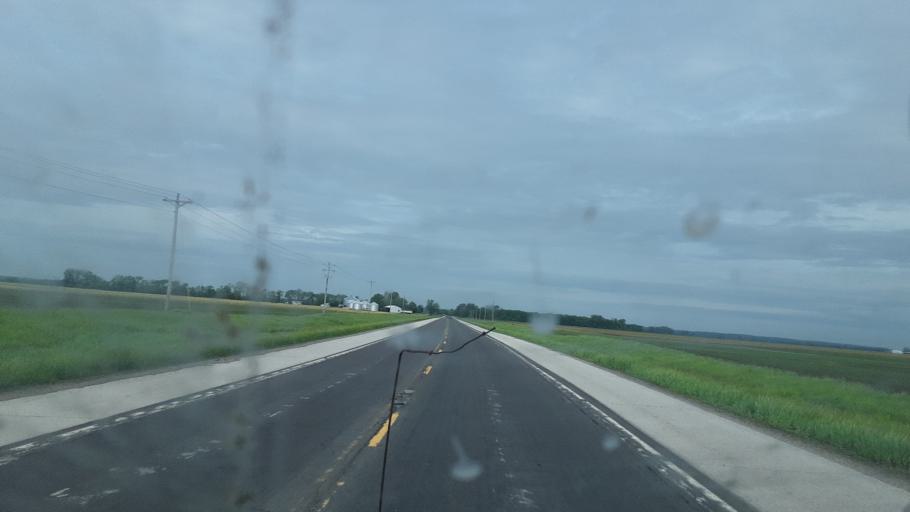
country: US
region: Illinois
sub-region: Hancock County
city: Warsaw
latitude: 40.3844
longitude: -91.5044
